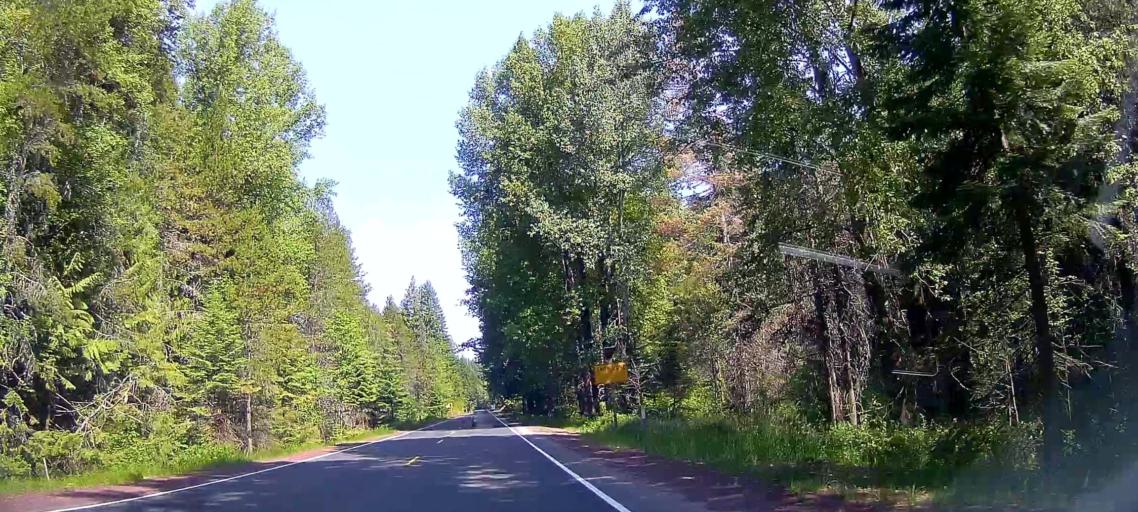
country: US
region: Oregon
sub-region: Clackamas County
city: Mount Hood Village
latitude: 45.1206
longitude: -121.5829
